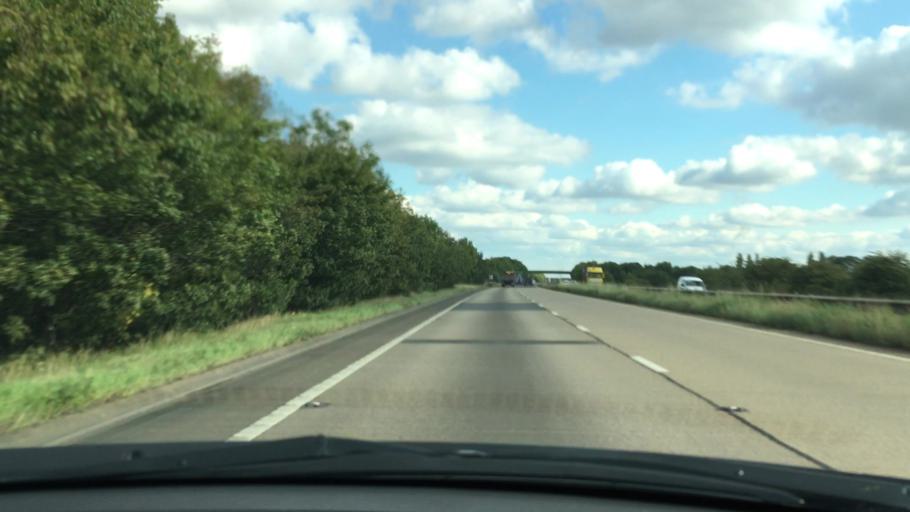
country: GB
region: England
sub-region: North East Lincolnshire
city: Healing
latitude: 53.5912
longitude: -0.1634
